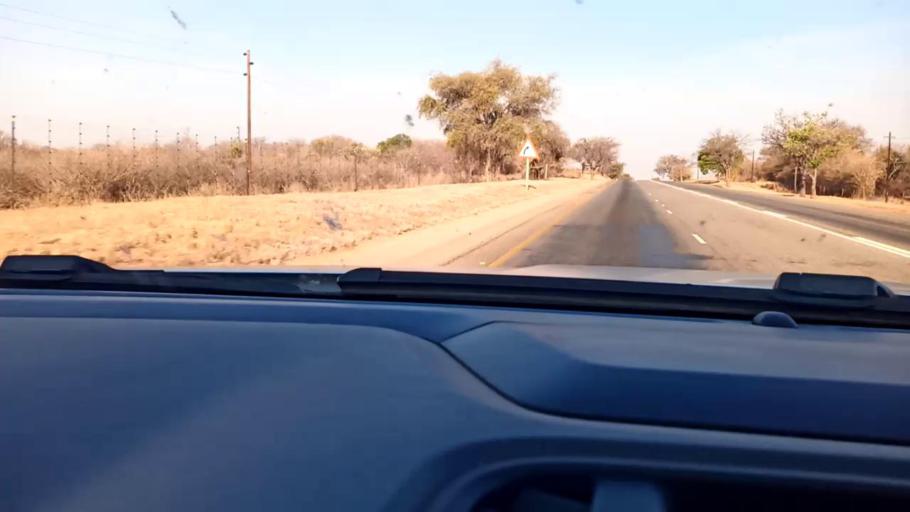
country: ZA
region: Limpopo
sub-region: Mopani District Municipality
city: Duiwelskloof
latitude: -23.6191
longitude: 30.1229
